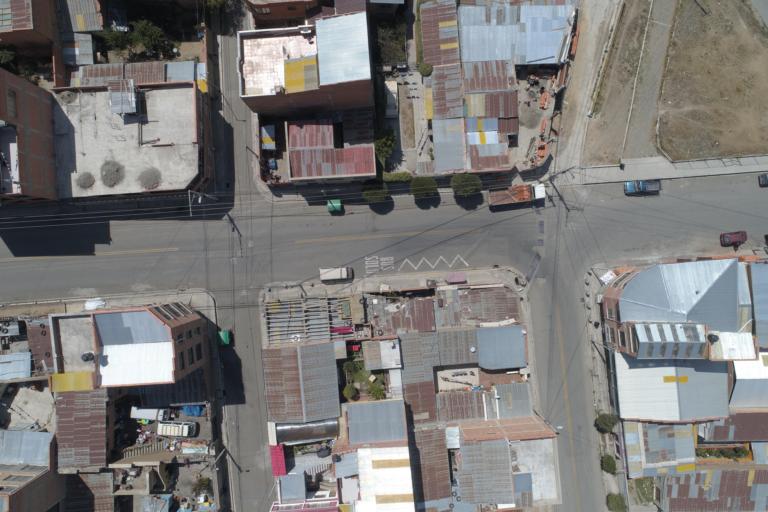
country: BO
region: La Paz
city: La Paz
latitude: -16.4990
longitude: -68.1012
